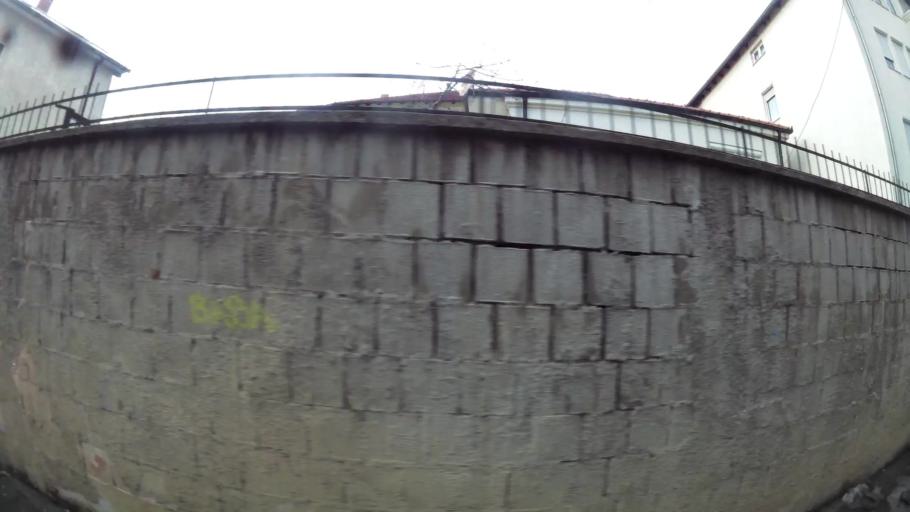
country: XK
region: Pristina
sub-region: Komuna e Prishtines
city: Pristina
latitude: 42.6725
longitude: 21.1686
